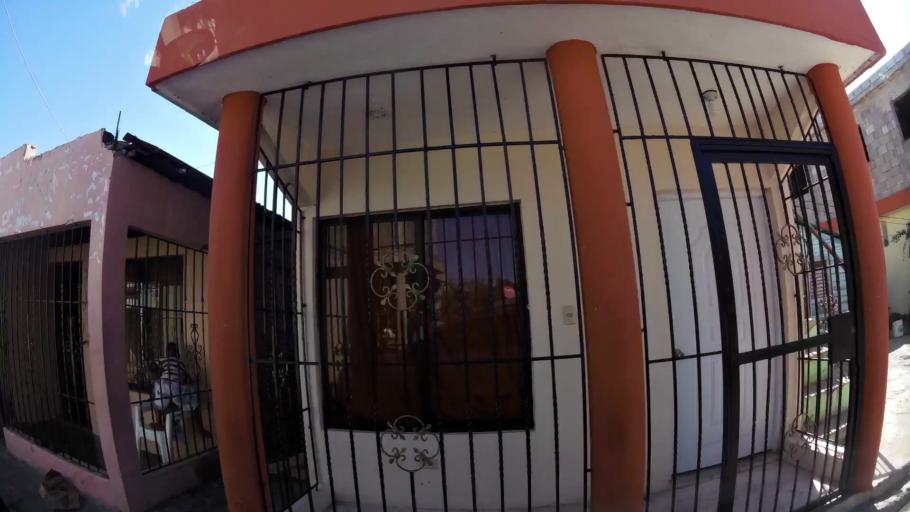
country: DO
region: San Cristobal
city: San Cristobal
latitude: 18.4325
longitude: -70.1169
